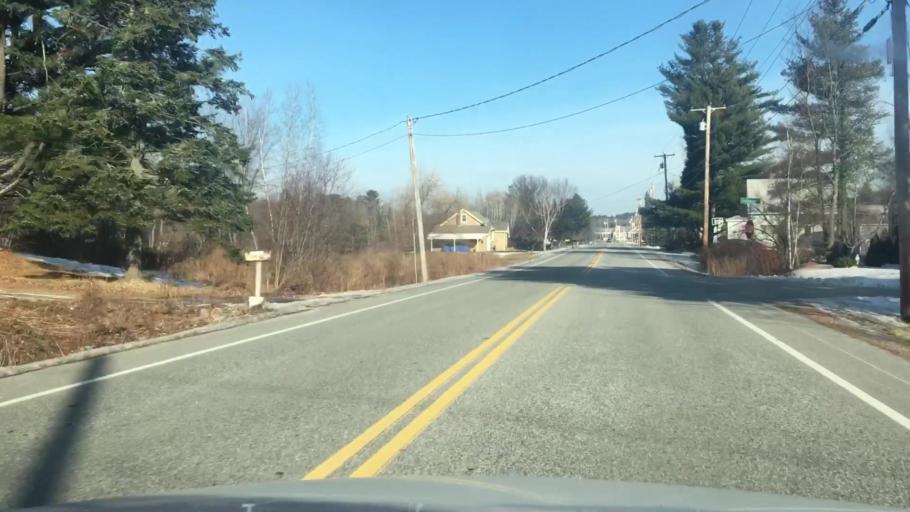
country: US
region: Maine
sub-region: Androscoggin County
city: Auburn
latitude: 44.0765
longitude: -70.2634
